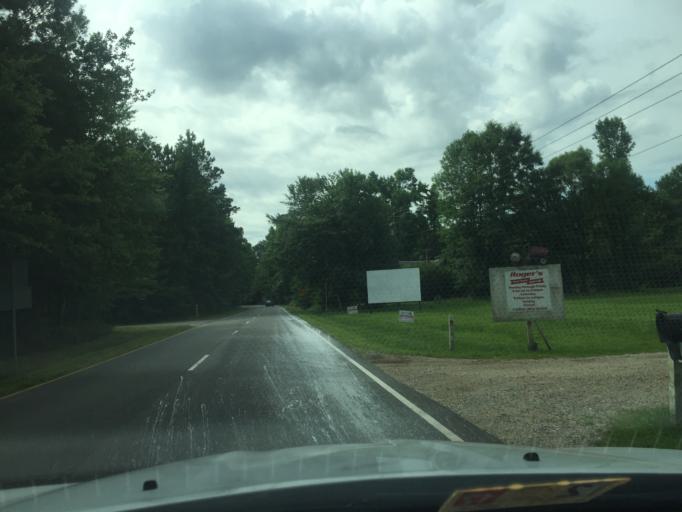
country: US
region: Virginia
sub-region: Charles City County
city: Charles City
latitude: 37.4519
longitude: -77.0783
